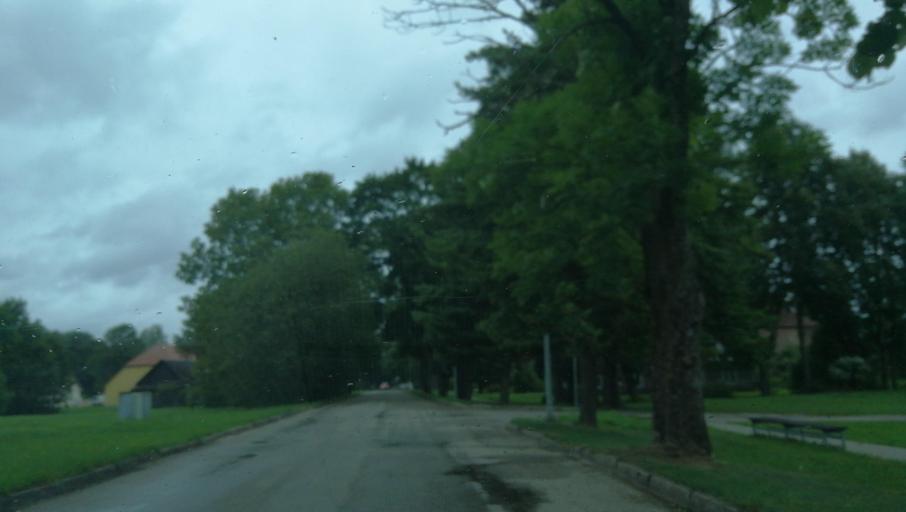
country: LV
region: Beverina
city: Murmuiza
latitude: 57.4736
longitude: 25.4913
